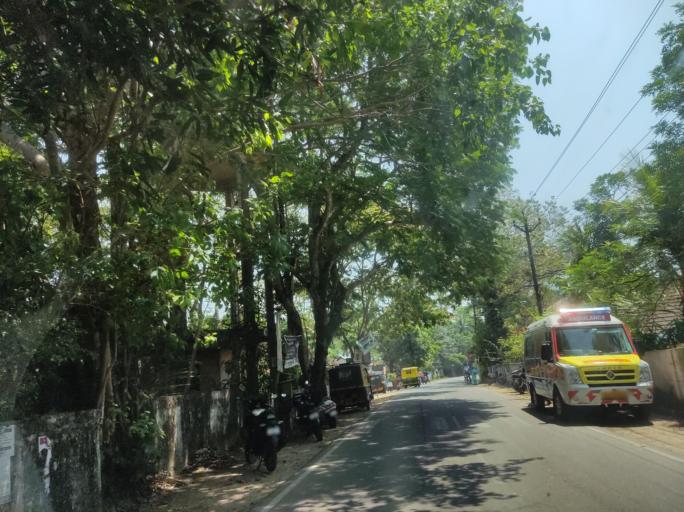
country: IN
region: Kerala
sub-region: Alappuzha
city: Kutiatodu
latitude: 9.8321
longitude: 76.2979
